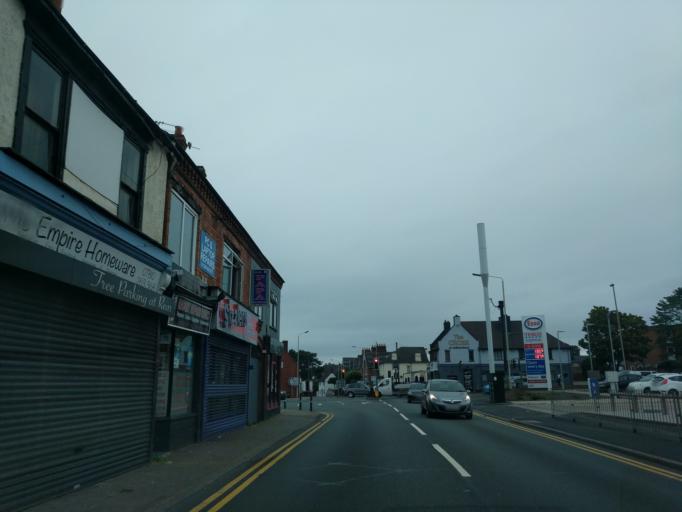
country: GB
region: England
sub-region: Dudley
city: Stourbridge
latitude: 52.4479
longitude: -2.1406
